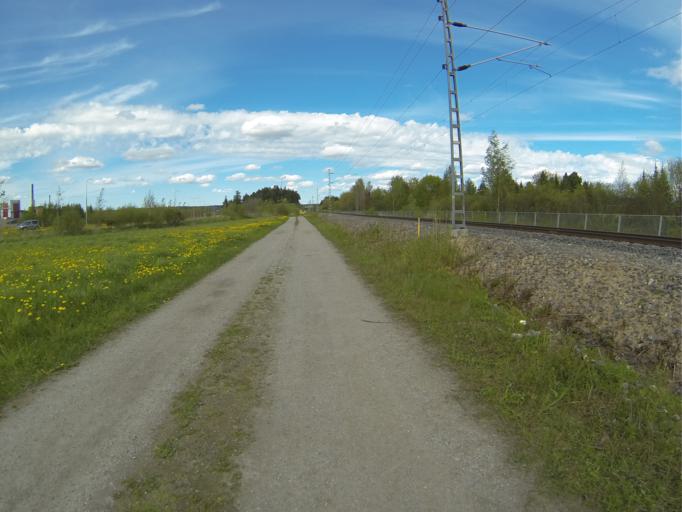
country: FI
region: Varsinais-Suomi
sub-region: Salo
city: Salo
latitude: 60.3664
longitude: 23.1187
